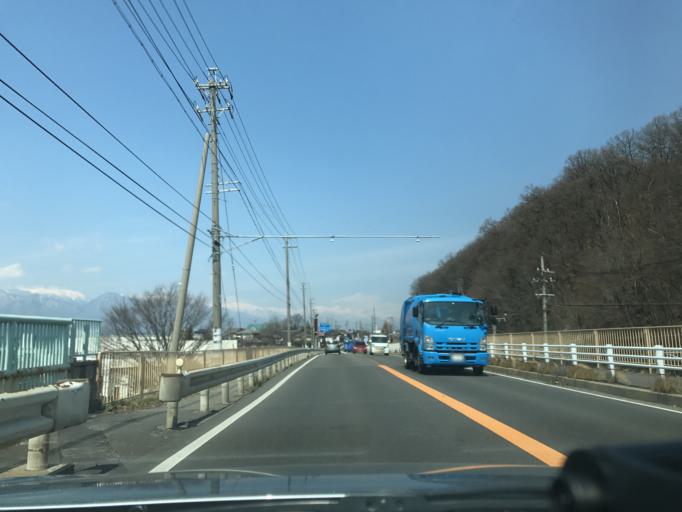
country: JP
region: Nagano
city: Matsumoto
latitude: 36.2424
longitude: 137.9540
